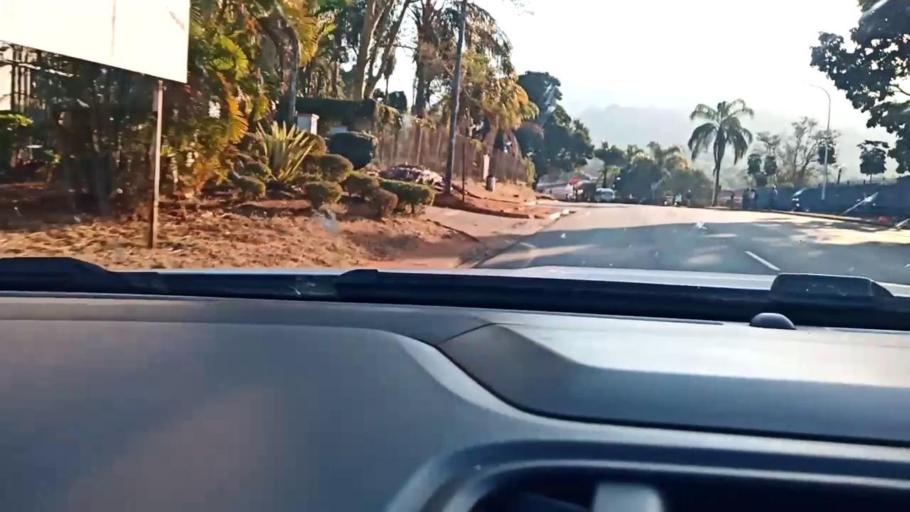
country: ZA
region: Limpopo
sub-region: Mopani District Municipality
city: Duiwelskloof
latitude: -23.6952
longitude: 30.1451
